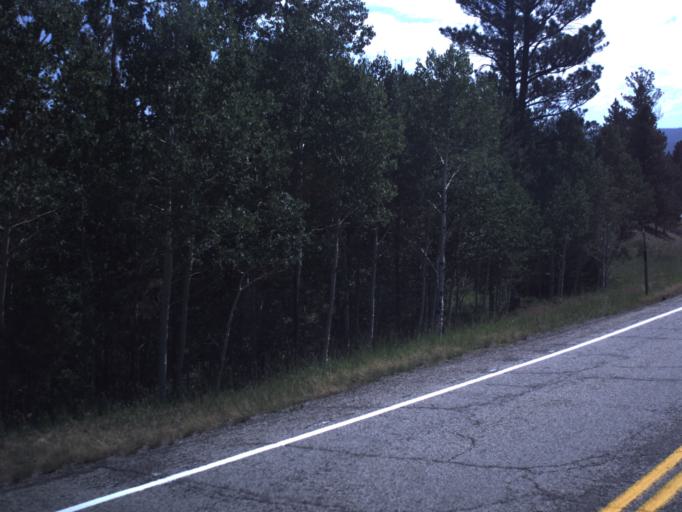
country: US
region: Utah
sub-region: Daggett County
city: Manila
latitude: 40.8499
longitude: -109.5870
